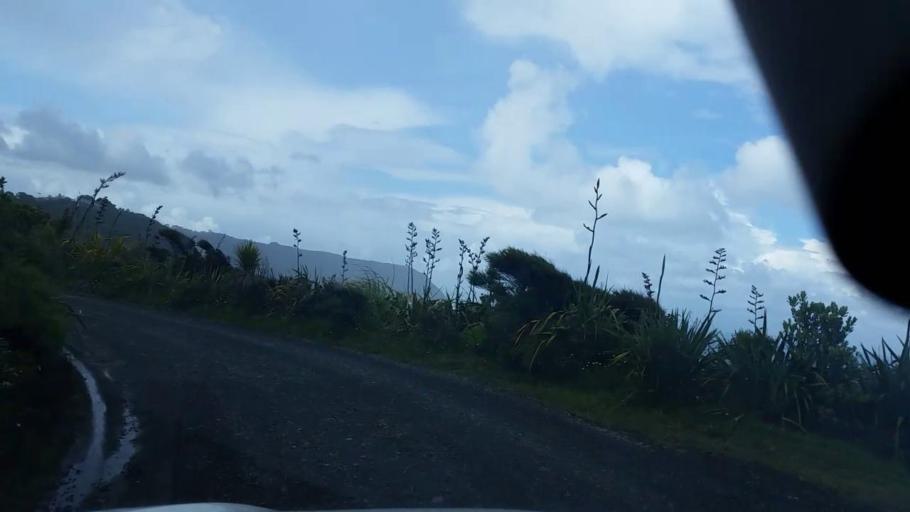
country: NZ
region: Auckland
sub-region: Auckland
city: Muriwai Beach
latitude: -36.9305
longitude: 174.4602
